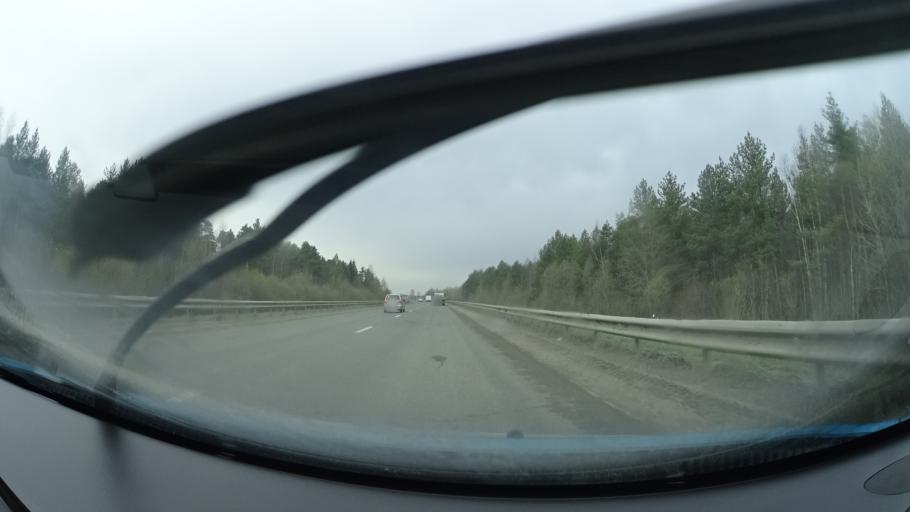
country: RU
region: Perm
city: Ust'-Kachka
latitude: 58.0821
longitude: 55.6647
